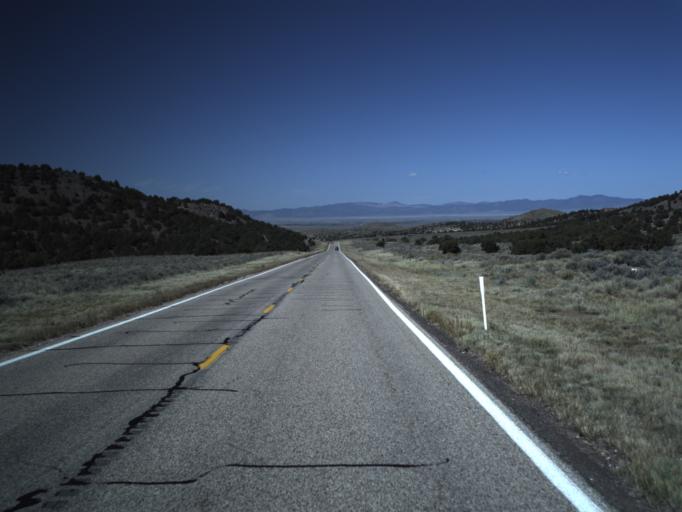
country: US
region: Utah
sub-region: Washington County
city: Enterprise
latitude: 37.6708
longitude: -113.4849
